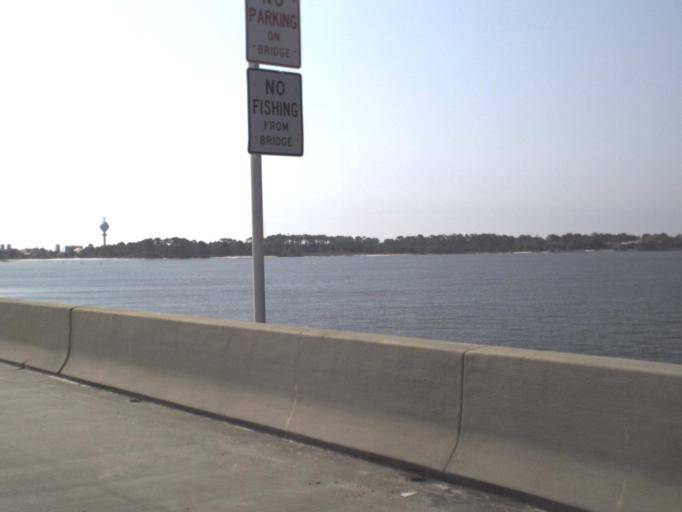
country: US
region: Florida
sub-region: Franklin County
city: Eastpoint
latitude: 29.6728
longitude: -84.8690
